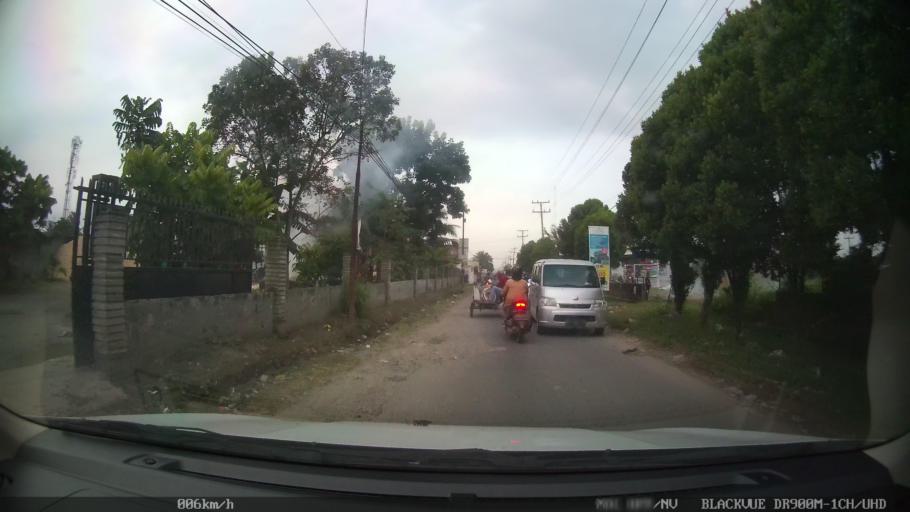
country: ID
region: North Sumatra
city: Sunggal
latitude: 3.5650
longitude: 98.5780
